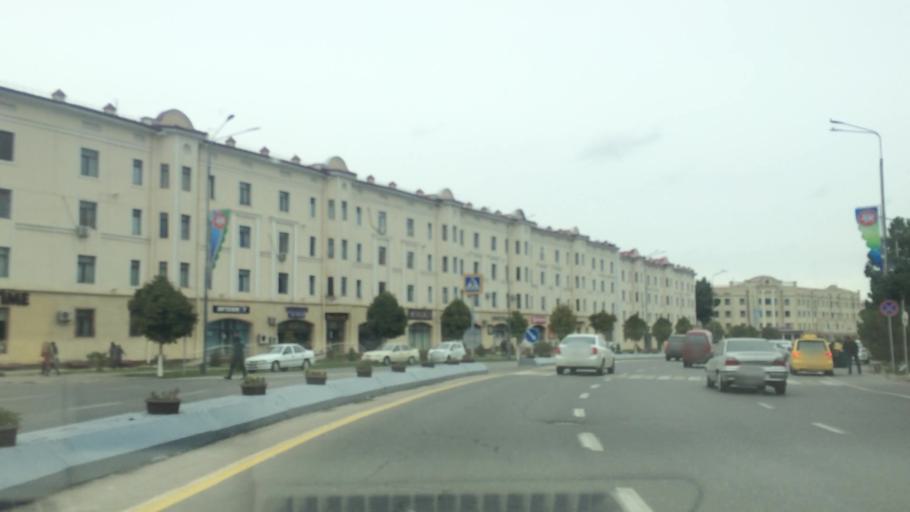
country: UZ
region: Samarqand
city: Samarqand
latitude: 39.6522
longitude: 66.9623
